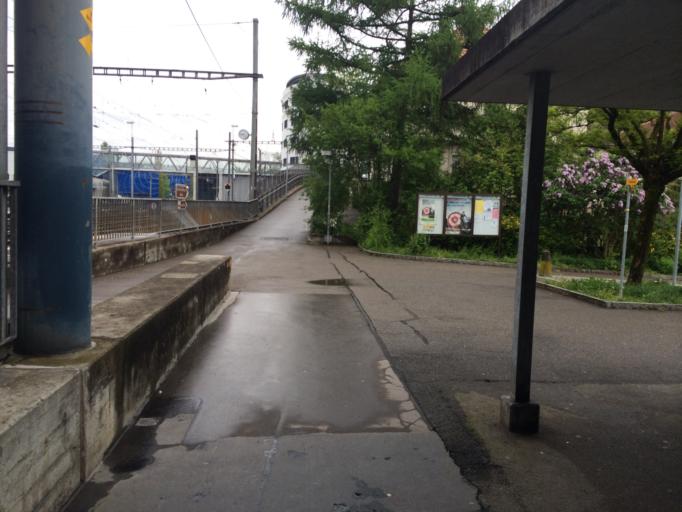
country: CH
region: Bern
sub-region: Bern-Mittelland District
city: Zollikofen
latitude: 46.9791
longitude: 7.4582
